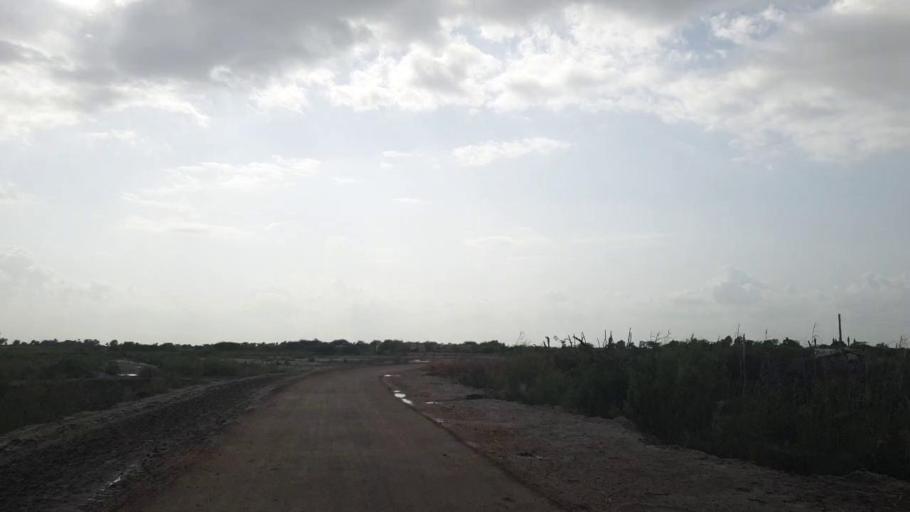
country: PK
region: Sindh
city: Kadhan
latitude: 24.5862
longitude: 69.0550
